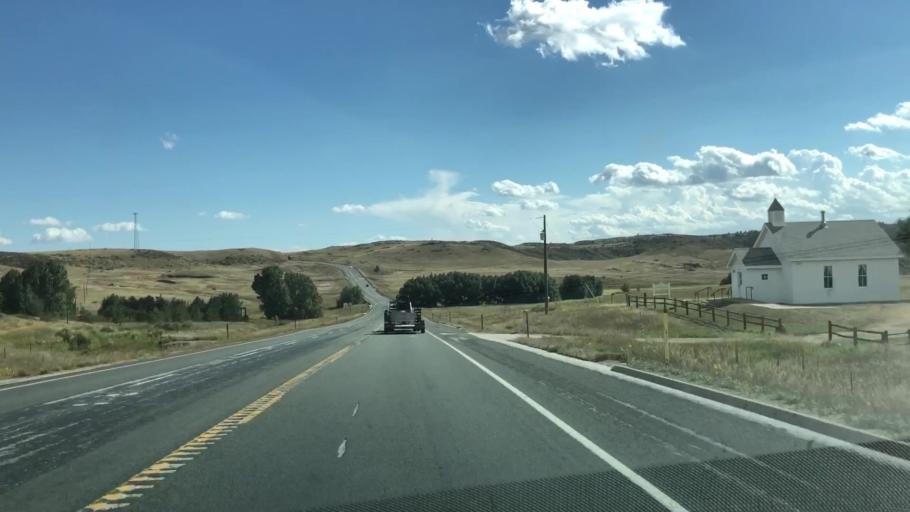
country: US
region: Colorado
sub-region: Larimer County
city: Laporte
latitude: 40.9401
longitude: -105.3428
